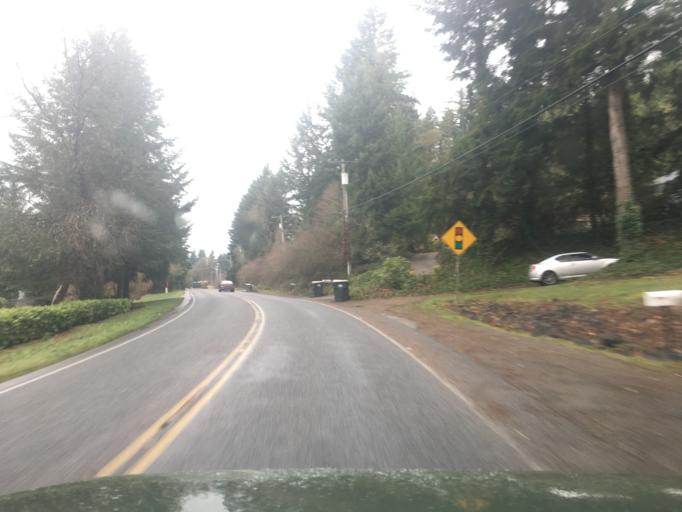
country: US
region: Washington
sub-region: Thurston County
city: Tanglewilde-Thompson Place
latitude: 47.0393
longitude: -122.7806
